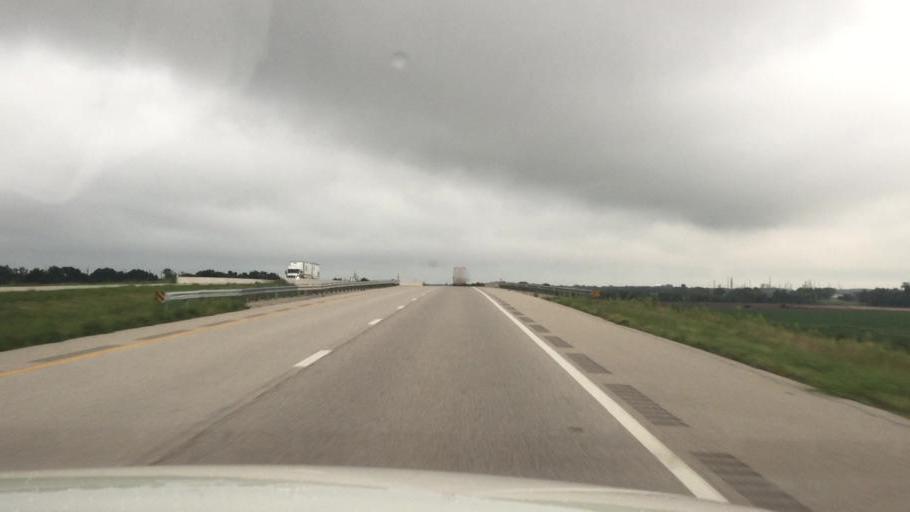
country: US
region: Kansas
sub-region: Montgomery County
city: Coffeyville
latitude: 37.0879
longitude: -95.5898
